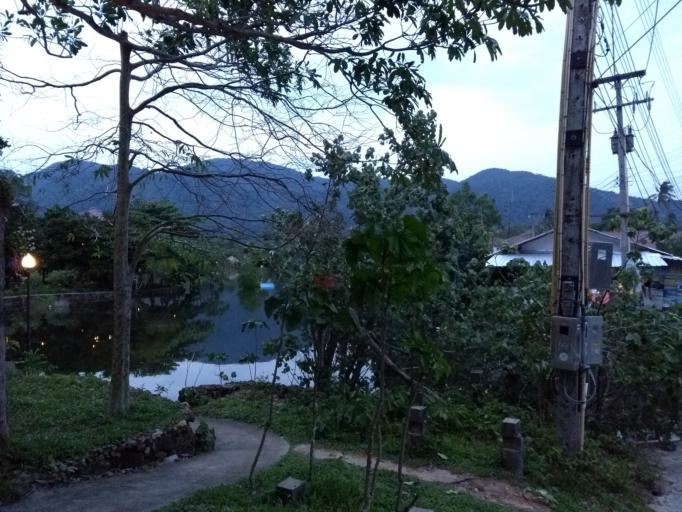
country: TH
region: Trat
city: Ko Chang Tai
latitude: 11.9748
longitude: 102.3220
